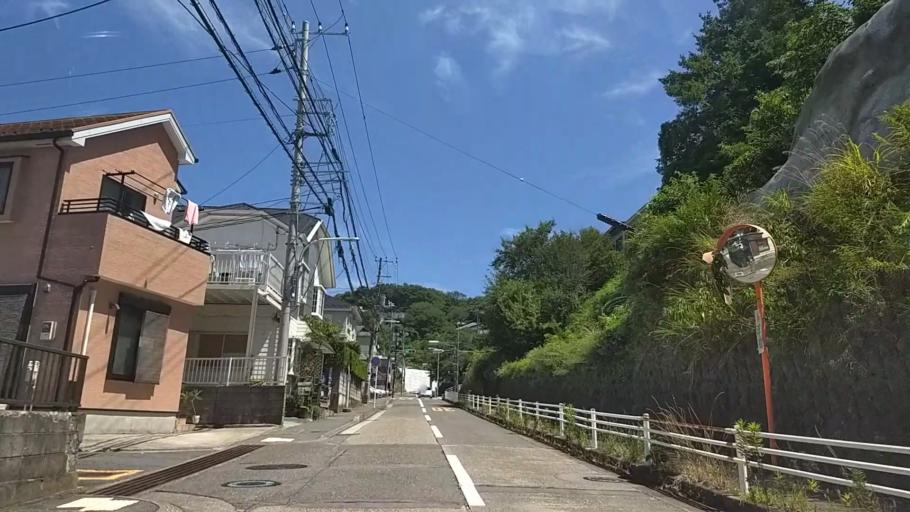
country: JP
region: Kanagawa
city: Zushi
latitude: 35.3046
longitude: 139.5975
